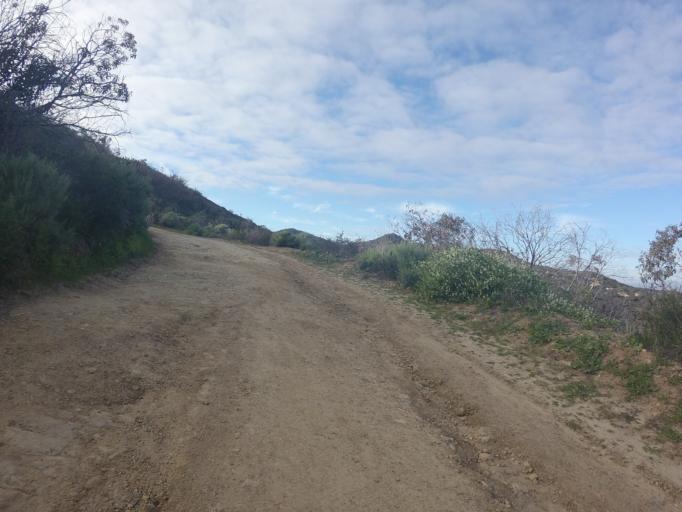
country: US
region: California
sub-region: Orange County
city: Aliso Viejo
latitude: 33.5852
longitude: -117.7657
